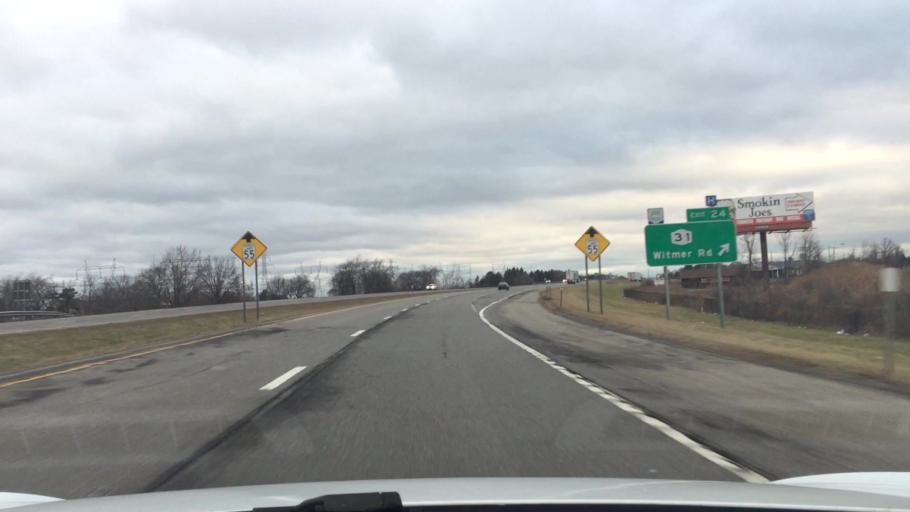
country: US
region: New York
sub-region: Niagara County
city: Lewiston
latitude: 43.1256
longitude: -79.0161
